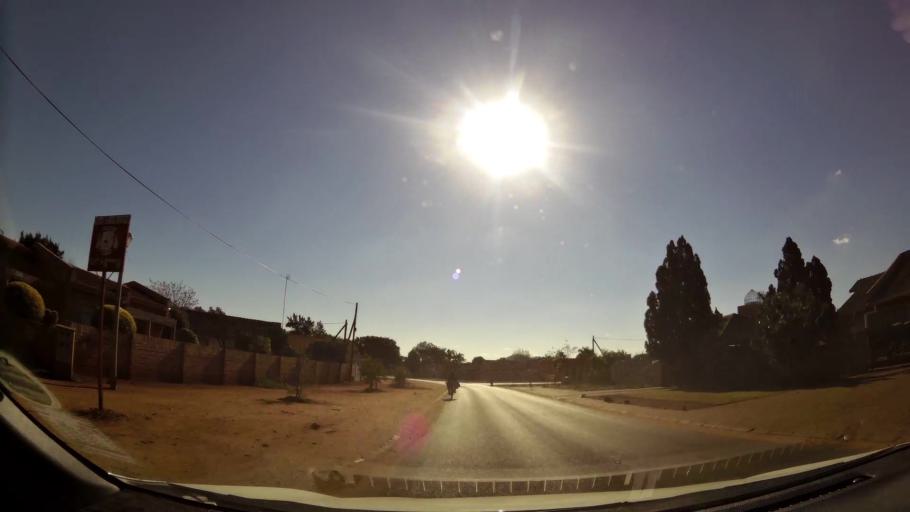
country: ZA
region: Limpopo
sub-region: Waterberg District Municipality
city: Mokopane
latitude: -24.1812
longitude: 28.9940
